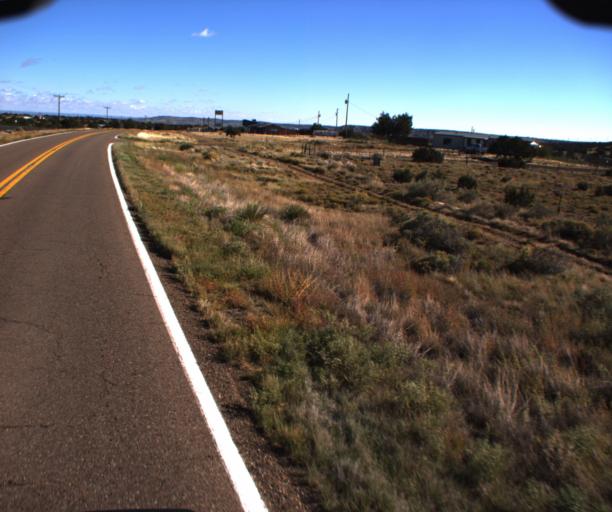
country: US
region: Arizona
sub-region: Apache County
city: Saint Johns
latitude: 34.4495
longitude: -109.6306
